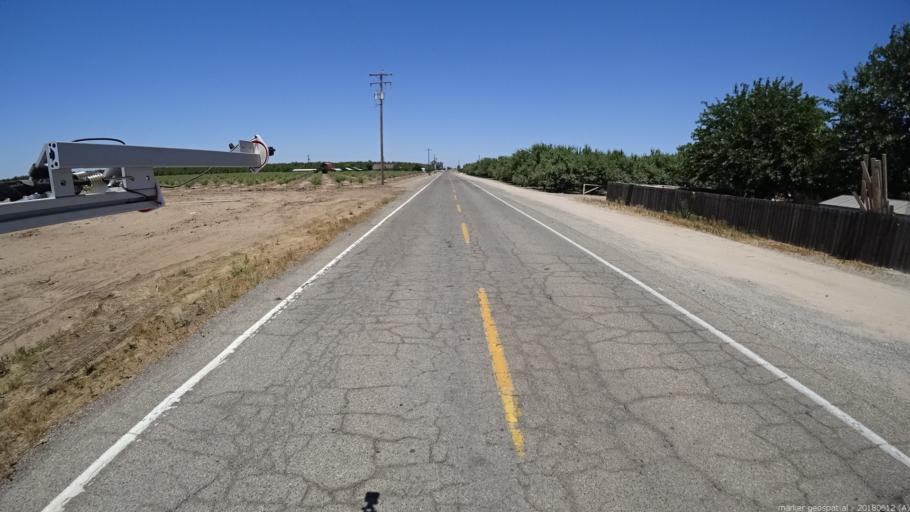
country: US
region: California
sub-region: Madera County
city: Chowchilla
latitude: 37.0781
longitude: -120.2568
